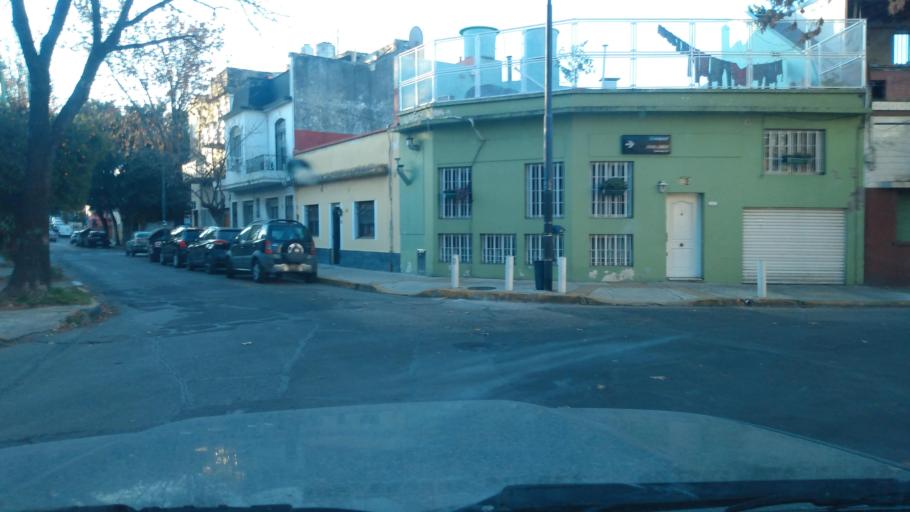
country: AR
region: Buenos Aires F.D.
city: Villa Santa Rita
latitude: -34.5827
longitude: -58.4821
